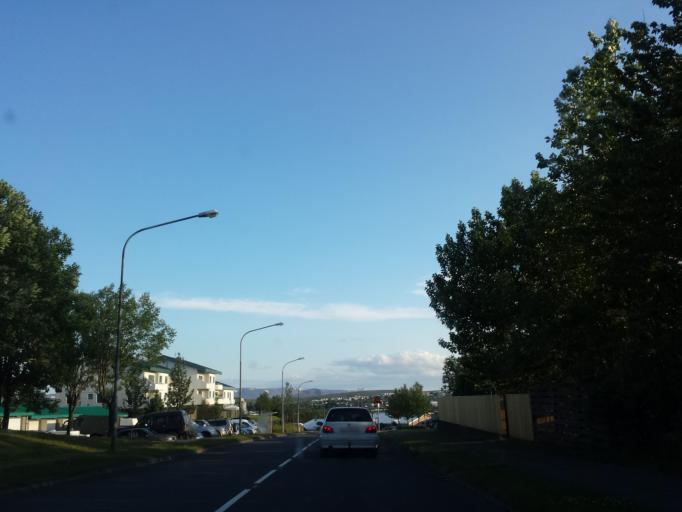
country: IS
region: Capital Region
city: Mosfellsbaer
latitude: 64.1087
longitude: -21.7879
